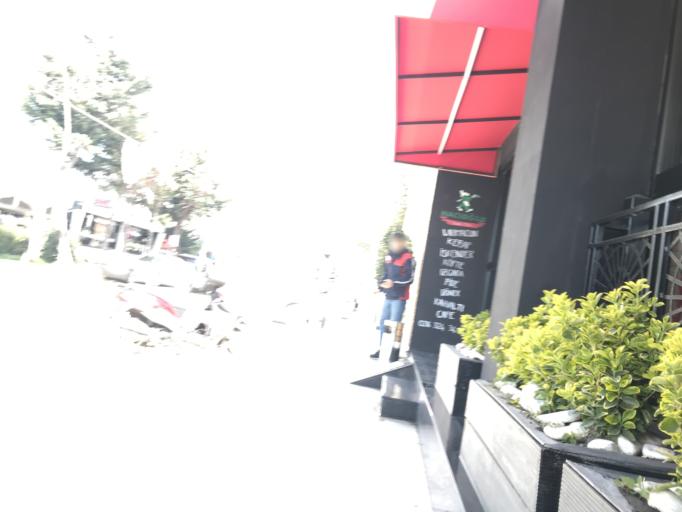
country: TR
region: Istanbul
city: Maltepe
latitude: 40.9246
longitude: 29.1257
